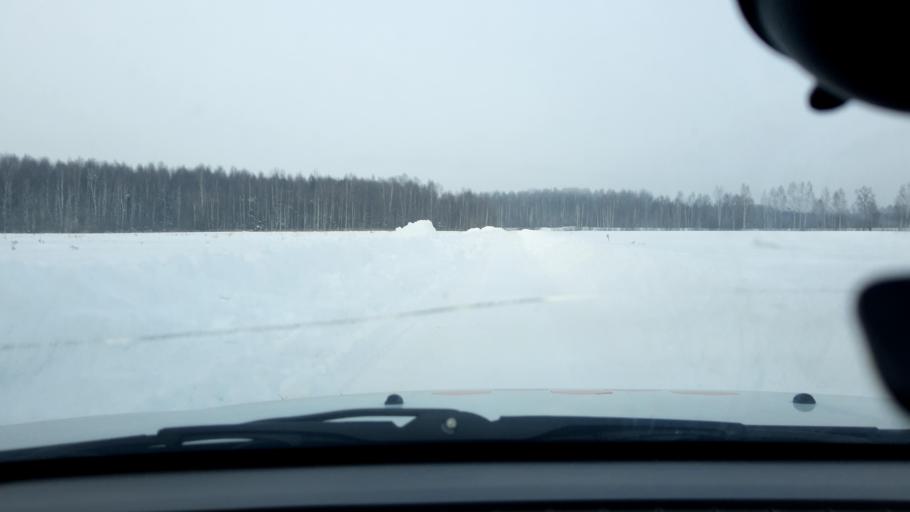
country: RU
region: Nizjnij Novgorod
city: Lukino
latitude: 56.5370
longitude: 43.7698
